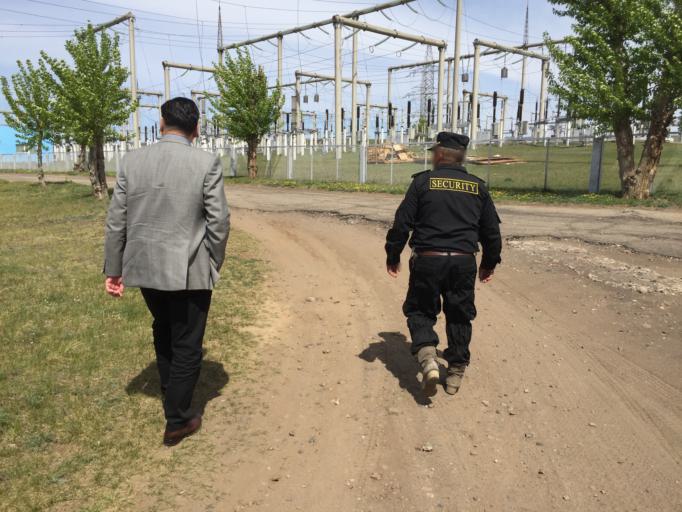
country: MN
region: Darhan Uul
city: Darhan
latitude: 49.3962
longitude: 105.9471
